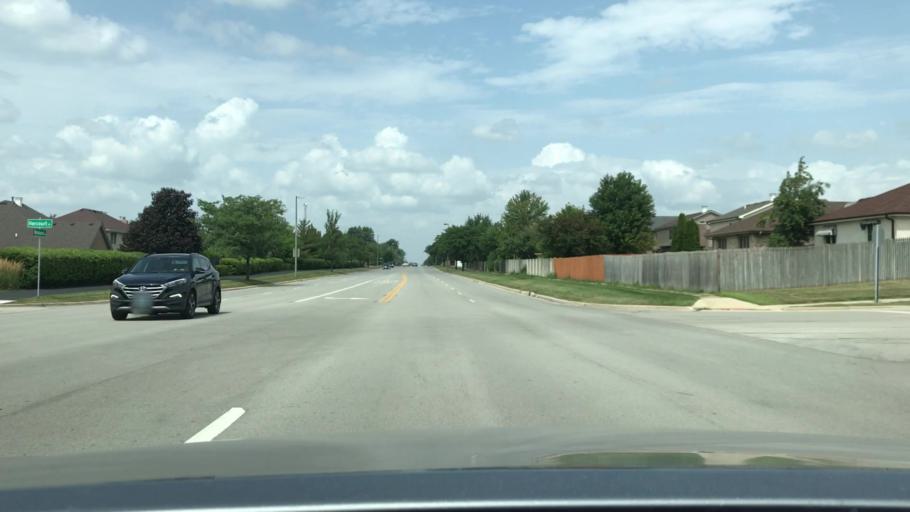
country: US
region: Illinois
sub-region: DuPage County
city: Woodridge
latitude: 41.7395
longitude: -88.0307
